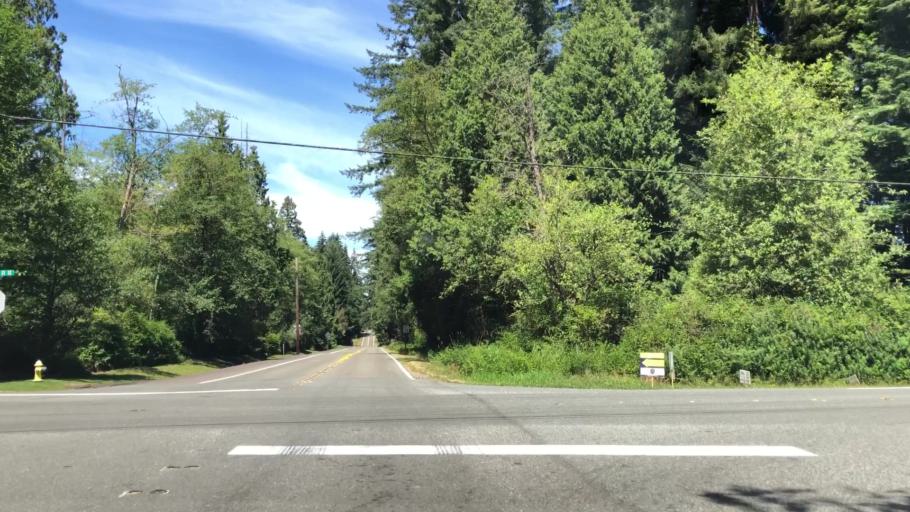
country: US
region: Washington
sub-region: Snohomish County
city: North Creek
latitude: 47.8341
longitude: -122.1641
